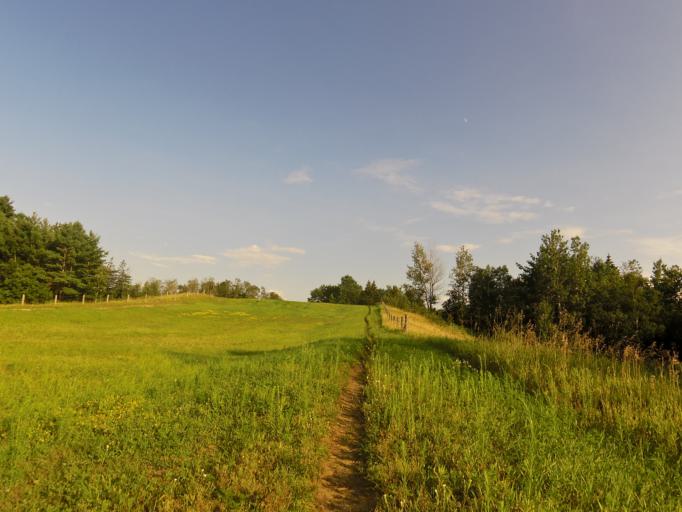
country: CA
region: Ontario
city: Bells Corners
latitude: 45.3256
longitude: -75.8046
